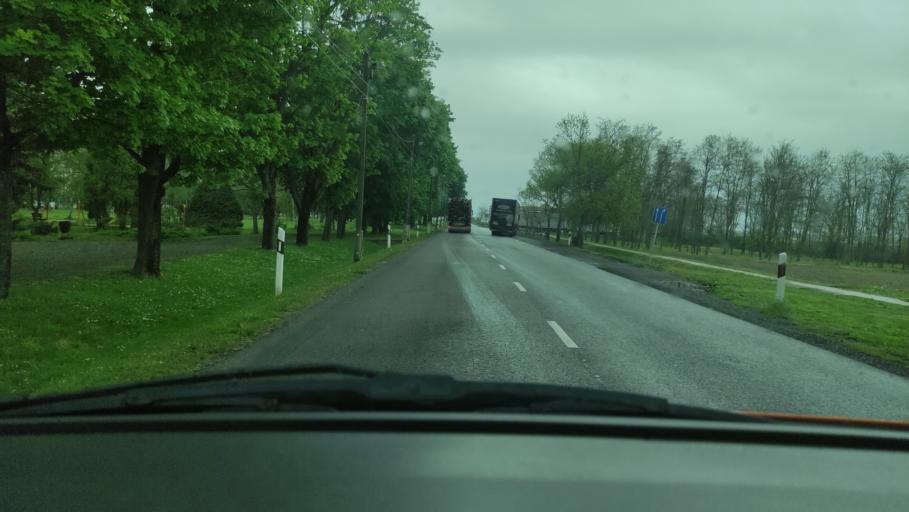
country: HU
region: Baranya
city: Mohacs
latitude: 45.9024
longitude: 18.6601
